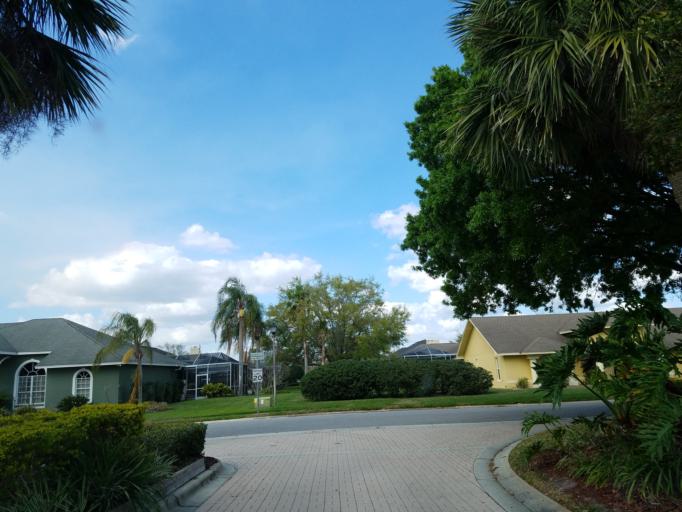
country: US
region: Florida
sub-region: Polk County
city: Lakeland Highlands
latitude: 27.9461
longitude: -81.9184
